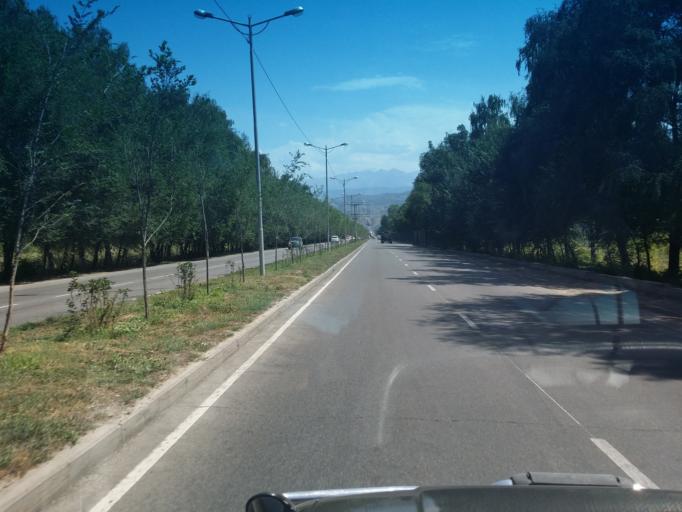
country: KZ
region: Almaty Oblysy
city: Pervomayskiy
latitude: 43.3228
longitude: 77.0209
